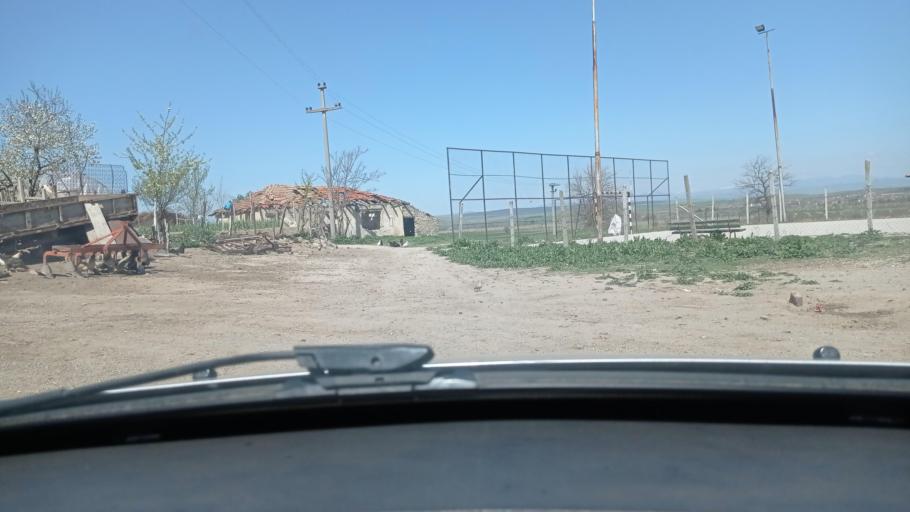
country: MK
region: Lozovo
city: Lozovo
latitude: 41.7641
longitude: 21.8684
